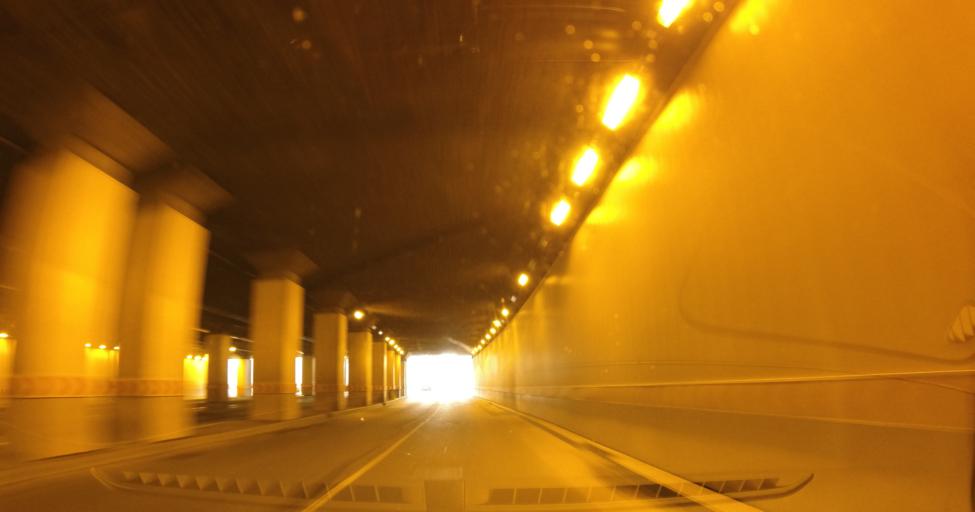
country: RO
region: Bucuresti
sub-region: Municipiul Bucuresti
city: Bucuresti
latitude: 44.4519
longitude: 26.0852
